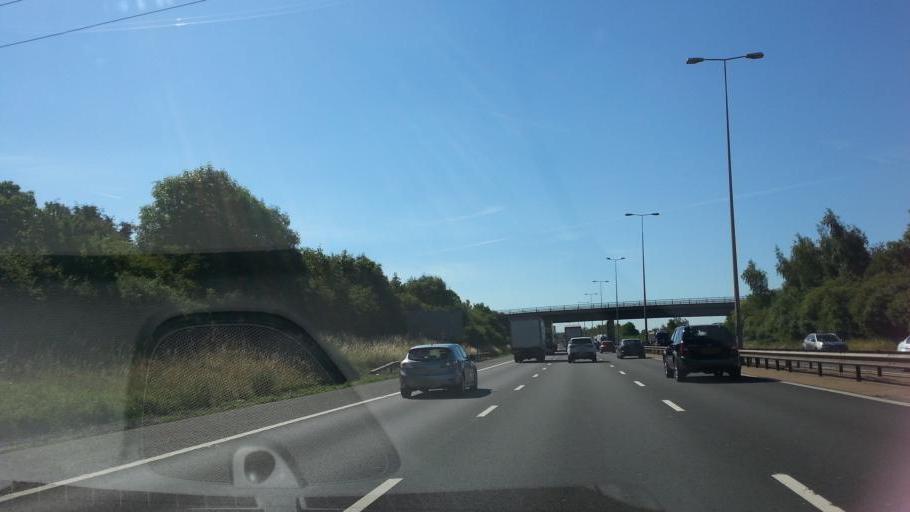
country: GB
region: England
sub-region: Worcestershire
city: Upton upon Severn
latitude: 52.0854
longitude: -2.1767
